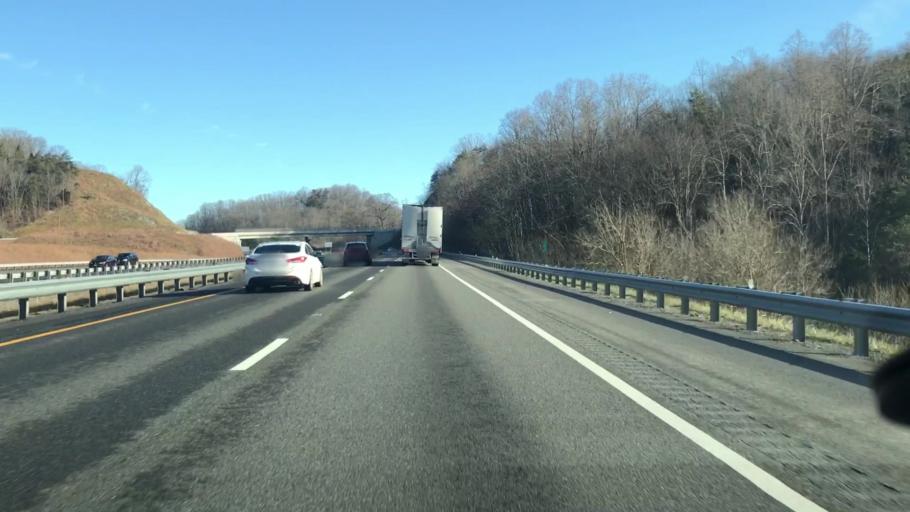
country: US
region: Virginia
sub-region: Montgomery County
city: Shawsville
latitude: 37.1934
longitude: -80.2719
